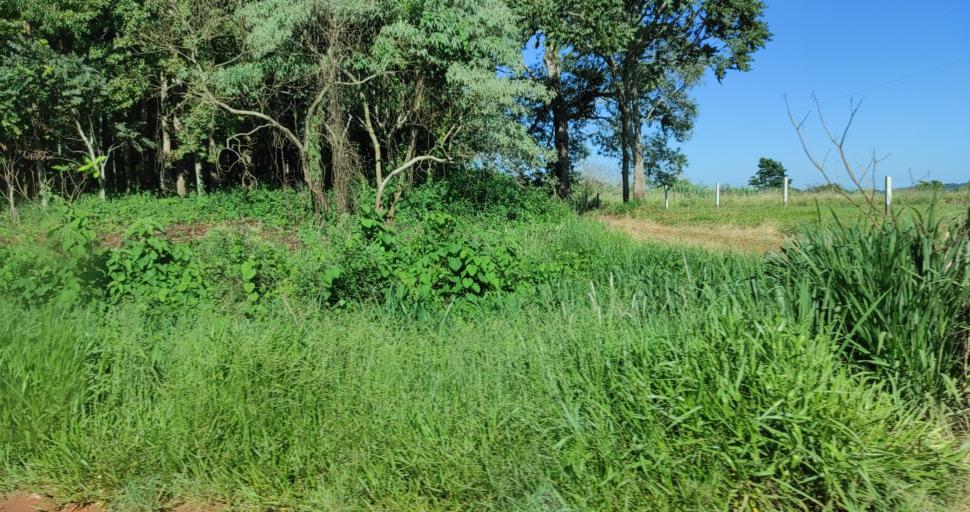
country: AR
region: Misiones
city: El Soberbio
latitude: -27.1902
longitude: -54.1071
